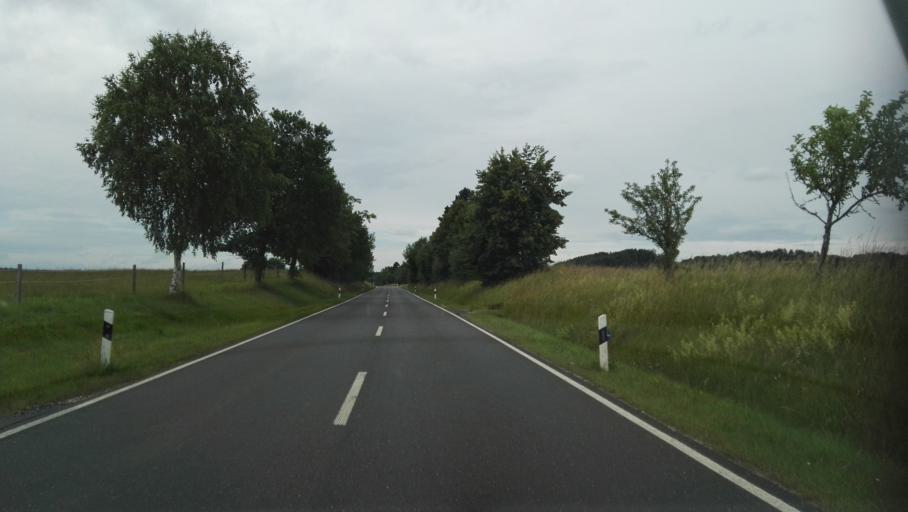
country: DE
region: Bavaria
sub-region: Upper Franconia
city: Plankenfels
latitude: 49.8901
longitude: 11.3358
